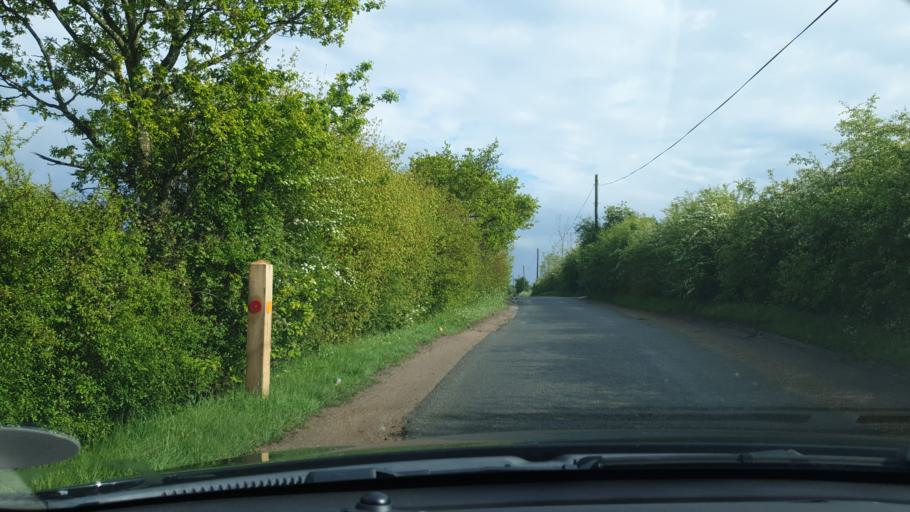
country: GB
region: England
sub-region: Essex
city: Great Bentley
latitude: 51.8389
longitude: 1.0513
